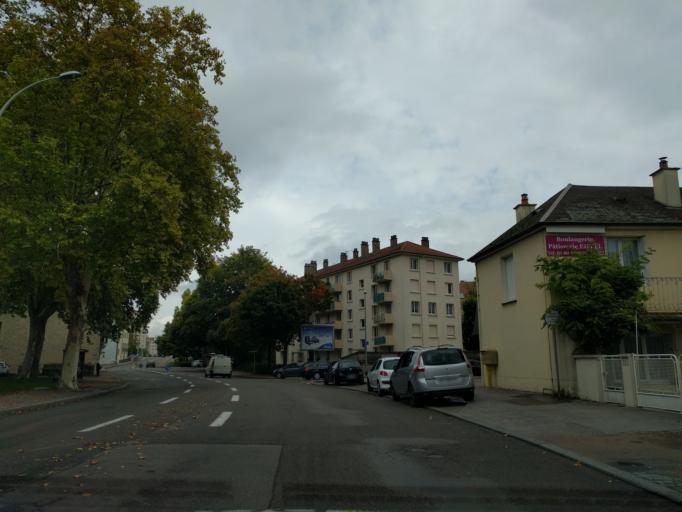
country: FR
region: Bourgogne
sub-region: Departement de la Cote-d'Or
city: Dijon
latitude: 47.3149
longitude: 5.0232
